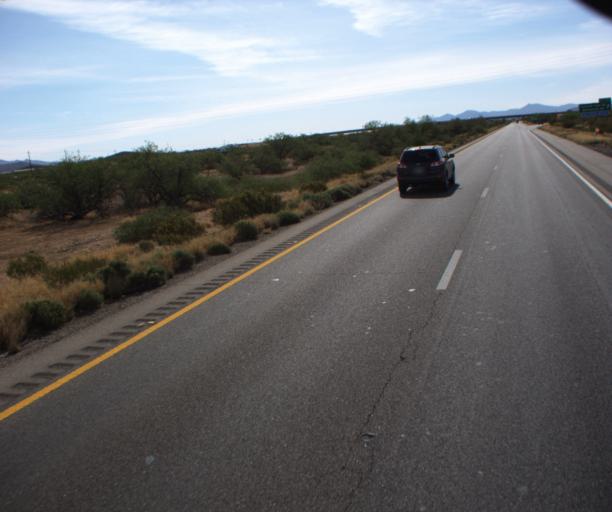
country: US
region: Arizona
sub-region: Pima County
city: Vail
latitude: 32.0302
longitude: -110.7254
